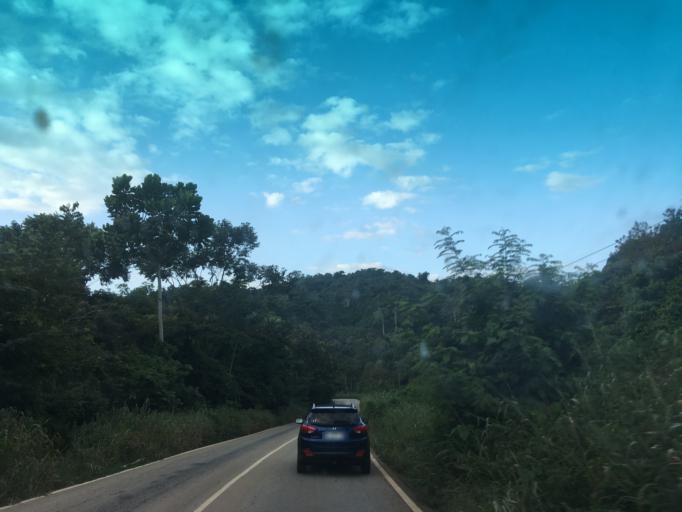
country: GH
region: Western
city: Bibiani
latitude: 6.4775
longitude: -2.3327
